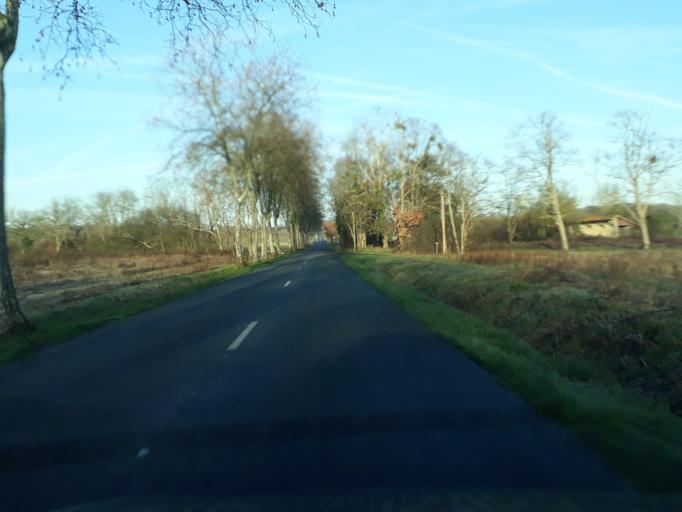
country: FR
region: Midi-Pyrenees
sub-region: Departement de la Haute-Garonne
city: Rieumes
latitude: 43.4268
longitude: 1.1366
